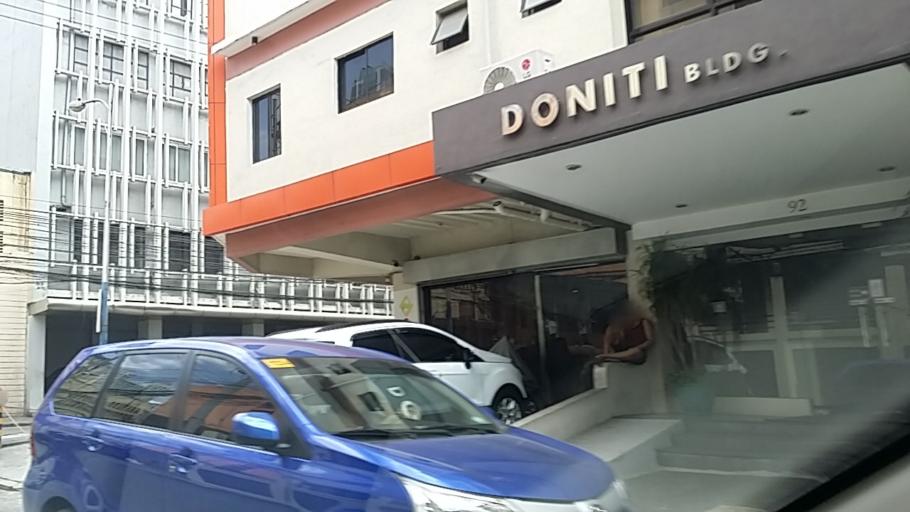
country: PH
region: Metro Manila
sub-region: Mandaluyong
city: Mandaluyong City
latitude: 14.5800
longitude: 121.0516
